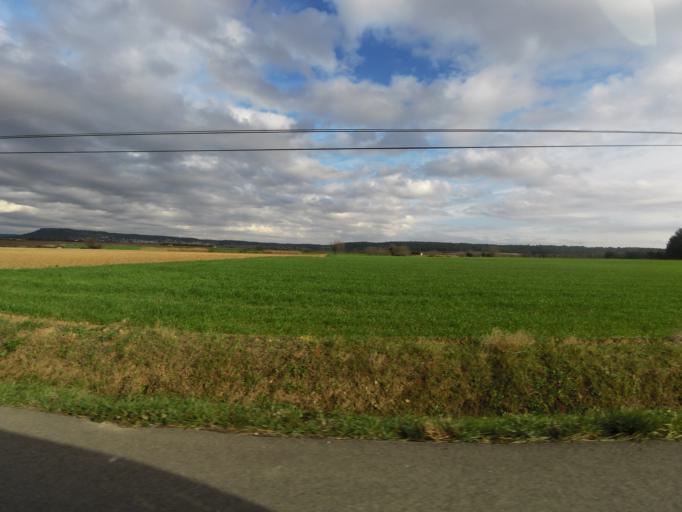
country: FR
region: Languedoc-Roussillon
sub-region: Departement du Gard
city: Mus
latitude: 43.7633
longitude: 4.2018
